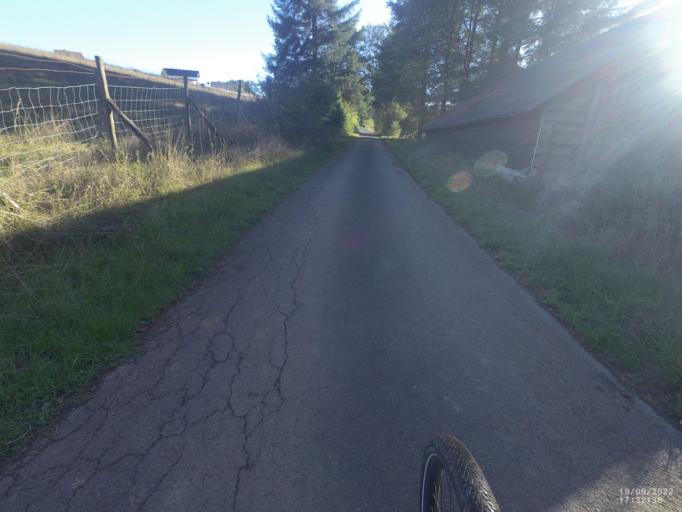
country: DE
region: Rheinland-Pfalz
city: Udersdorf
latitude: 50.1410
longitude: 6.8233
